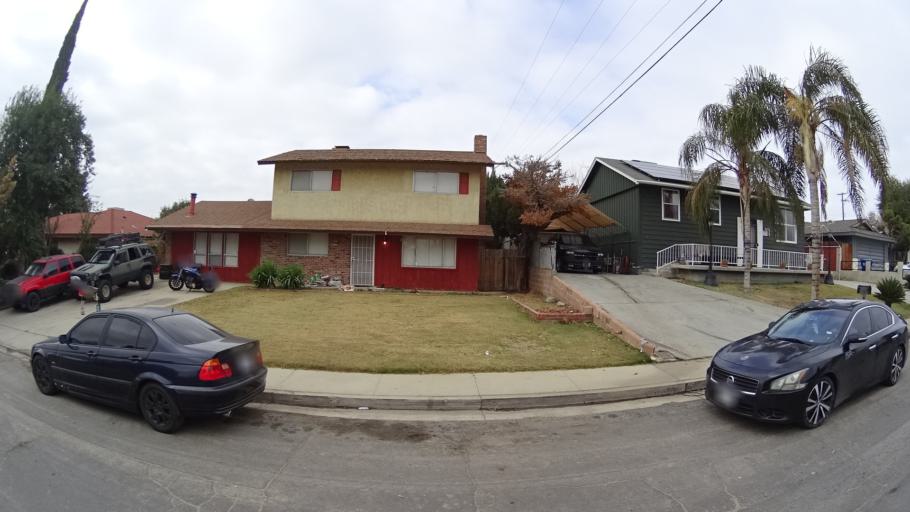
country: US
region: California
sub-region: Kern County
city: Bakersfield
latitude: 35.3785
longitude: -118.9159
